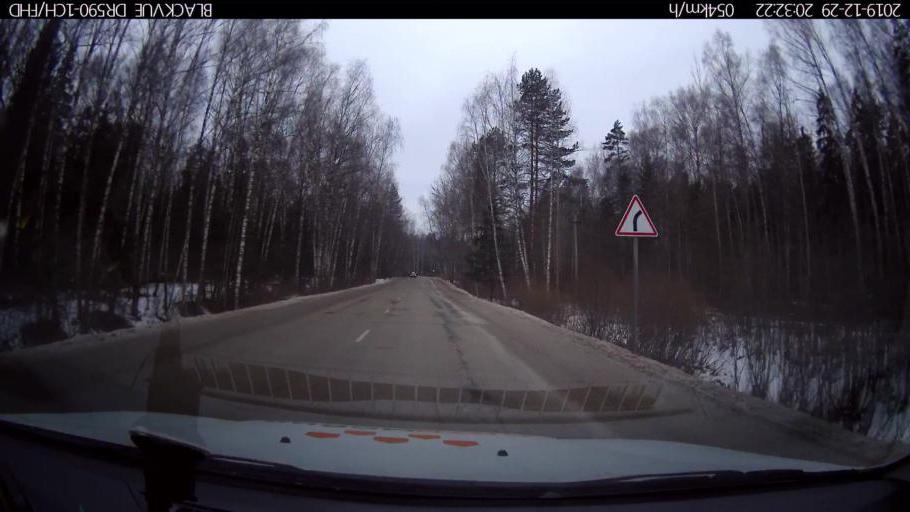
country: RU
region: Nizjnij Novgorod
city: Afonino
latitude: 56.1761
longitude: 44.0651
